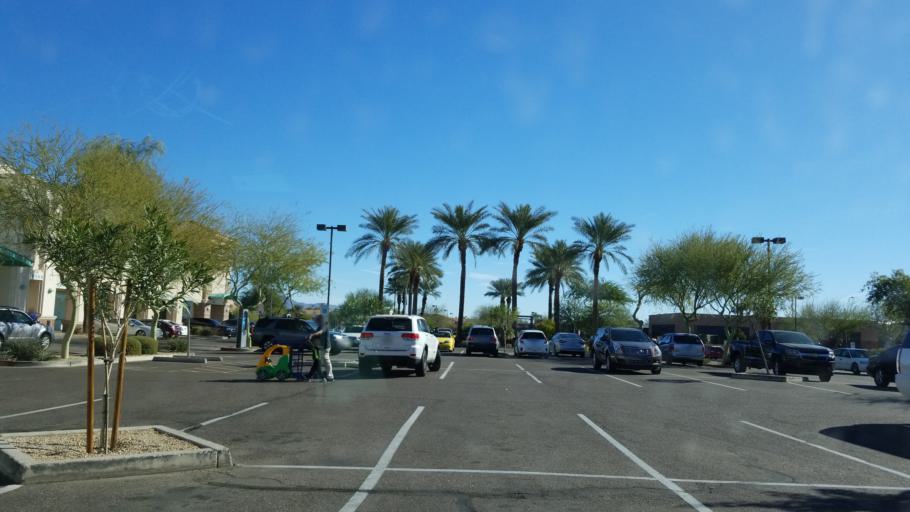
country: US
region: Arizona
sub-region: Maricopa County
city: Paradise Valley
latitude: 33.5847
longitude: -111.9796
